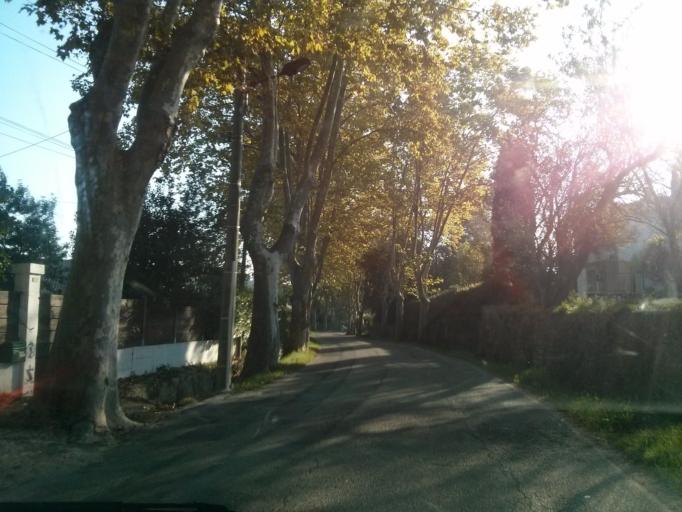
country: FR
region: Languedoc-Roussillon
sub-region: Departement du Gard
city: Aigues-Vives
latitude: 43.7331
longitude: 4.1851
